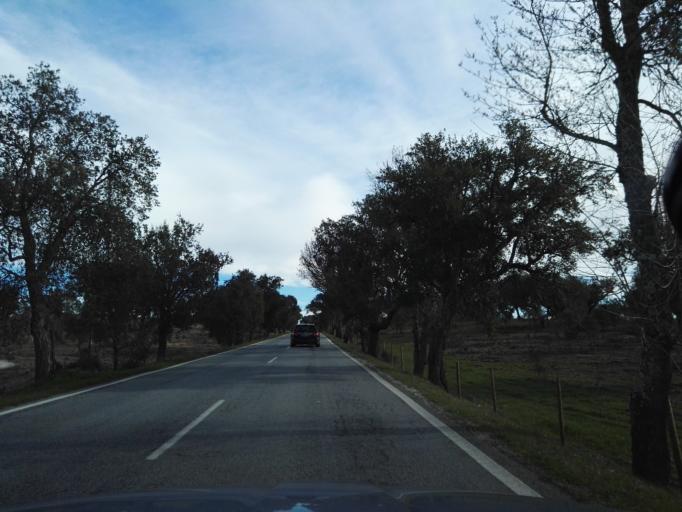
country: PT
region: Portalegre
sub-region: Nisa
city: Nisa
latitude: 39.4943
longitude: -7.7103
